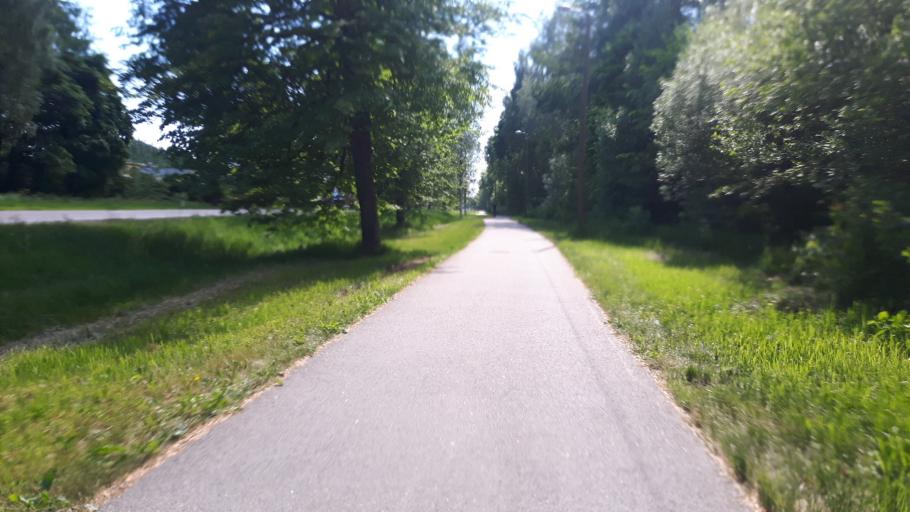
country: EE
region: Paernumaa
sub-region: Paikuse vald
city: Paikuse
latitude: 58.3829
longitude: 24.6346
